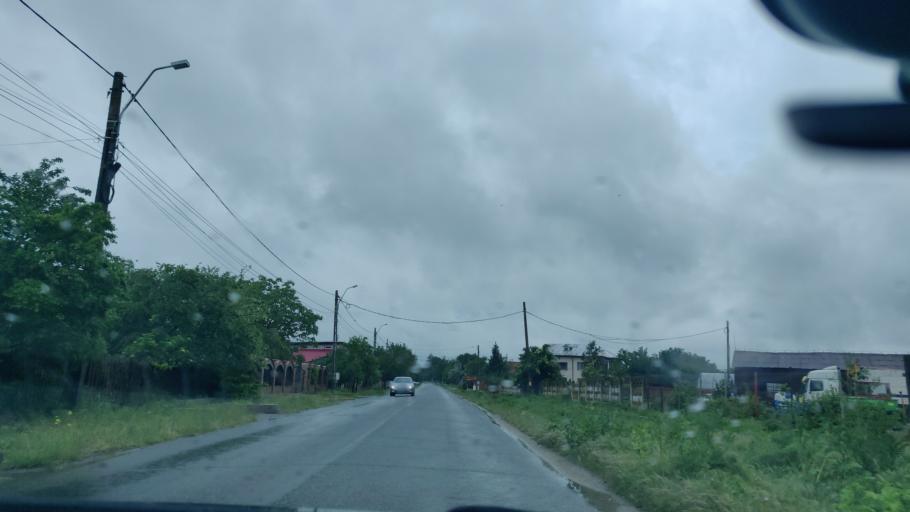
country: RO
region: Giurgiu
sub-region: Comuna Bulbucata
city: Bulbucata
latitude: 44.2734
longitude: 25.8301
